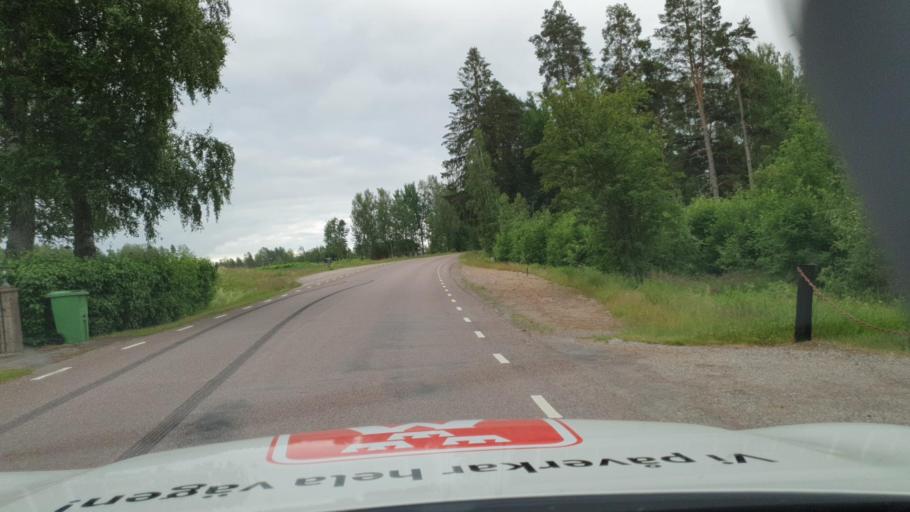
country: SE
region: Vaermland
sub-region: Kils Kommun
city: Kil
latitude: 59.5026
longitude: 13.3968
